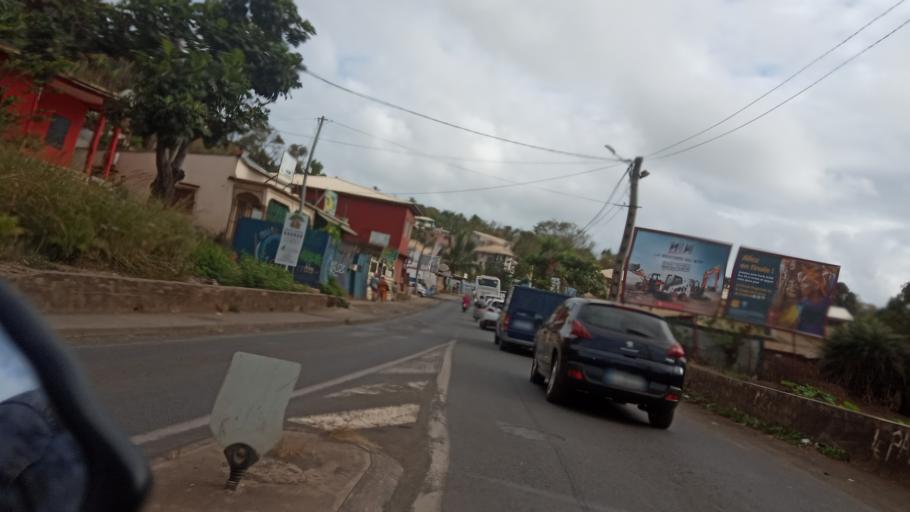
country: YT
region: Mamoudzou
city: Mamoudzou
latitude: -12.7872
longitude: 45.2255
